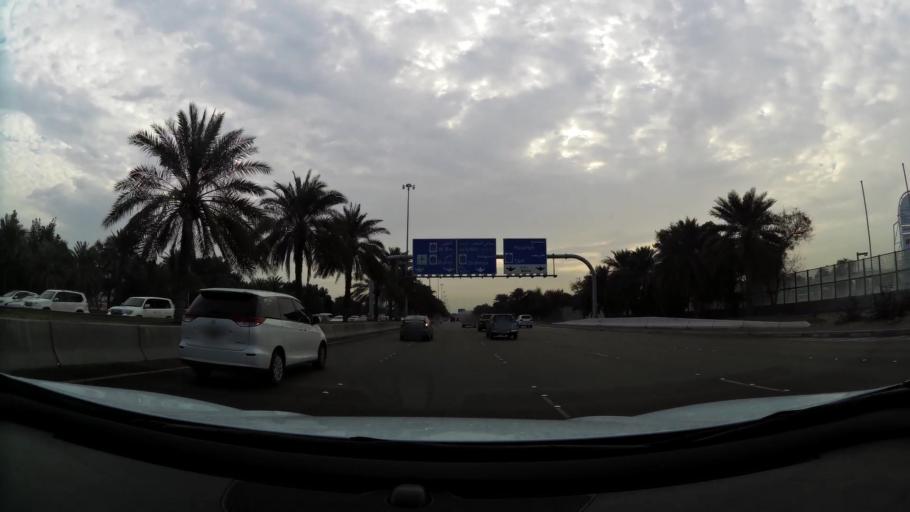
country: AE
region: Abu Dhabi
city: Abu Dhabi
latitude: 24.3969
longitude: 54.5091
